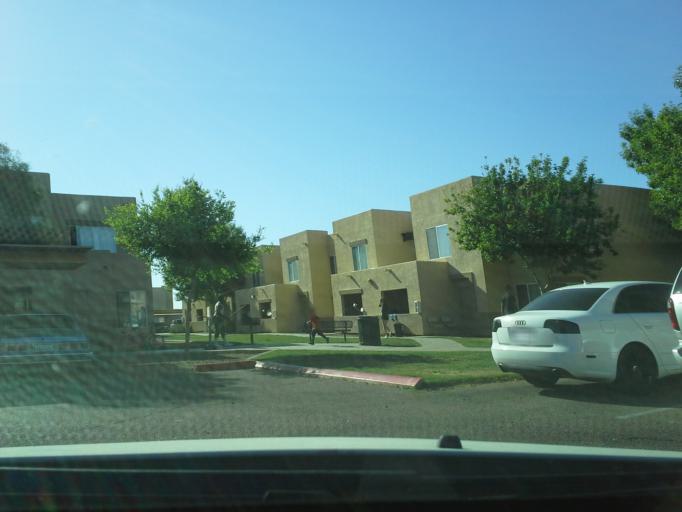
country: US
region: Arizona
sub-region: Maricopa County
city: Glendale
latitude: 33.5368
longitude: -112.2080
